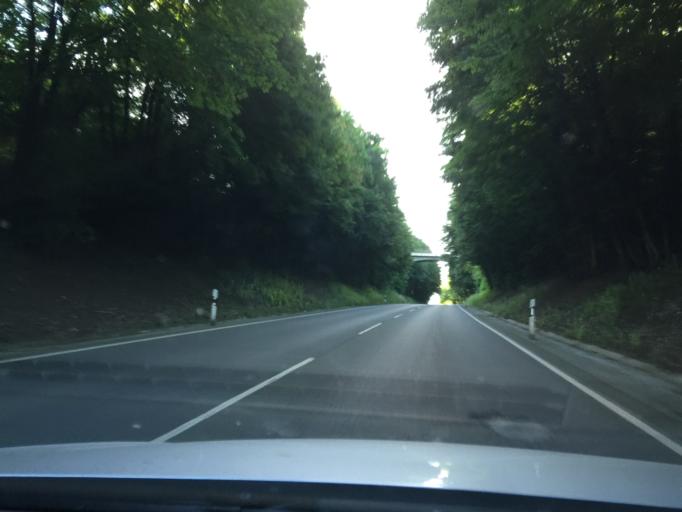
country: DE
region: North Rhine-Westphalia
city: Sprockhovel
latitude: 51.3371
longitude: 7.2179
